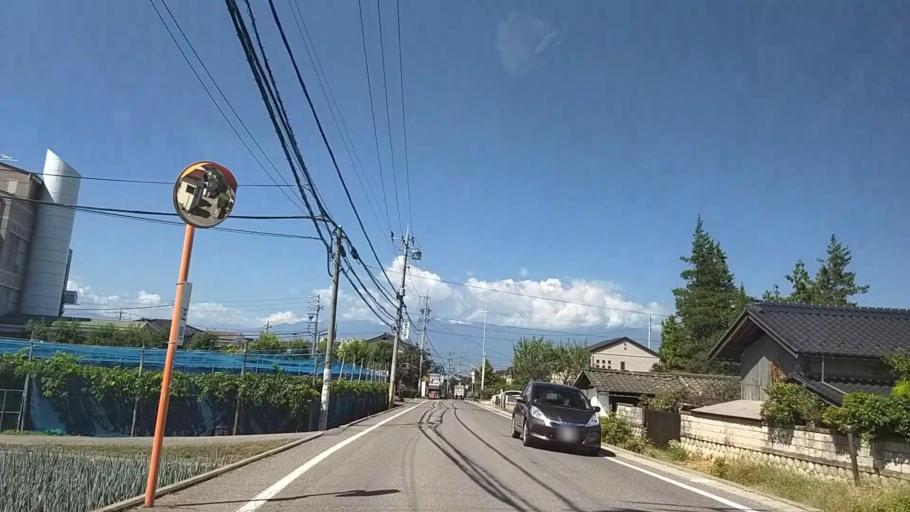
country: JP
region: Nagano
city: Matsumoto
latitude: 36.2359
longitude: 138.0009
